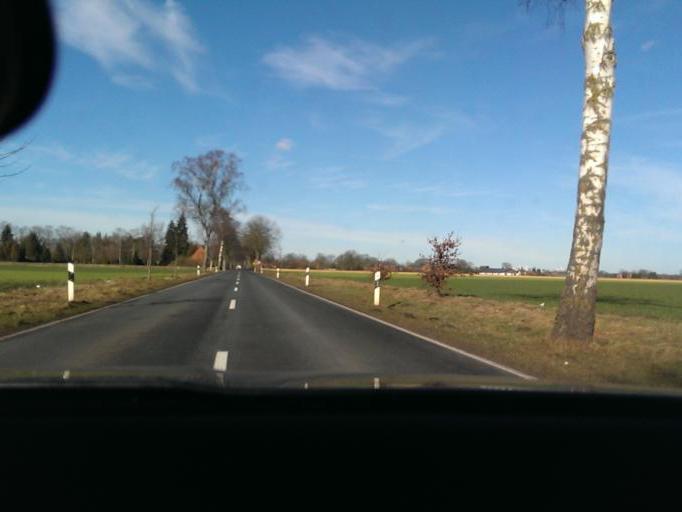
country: DE
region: Lower Saxony
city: Elze
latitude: 52.5764
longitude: 9.7459
